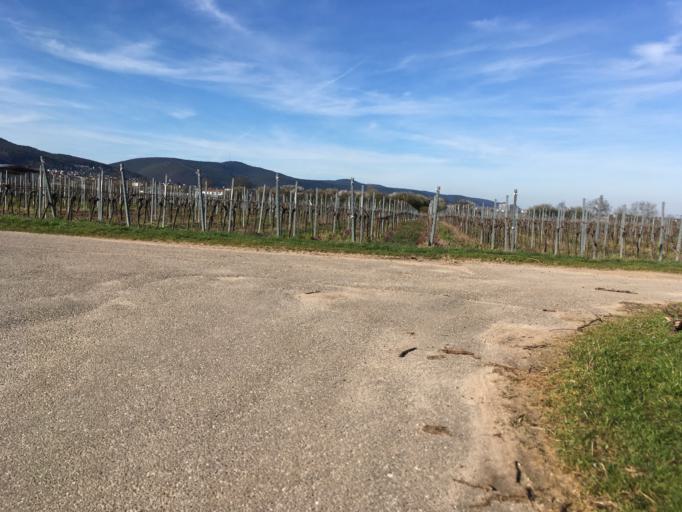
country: DE
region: Rheinland-Pfalz
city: Kirrweiler
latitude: 49.3171
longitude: 8.1523
